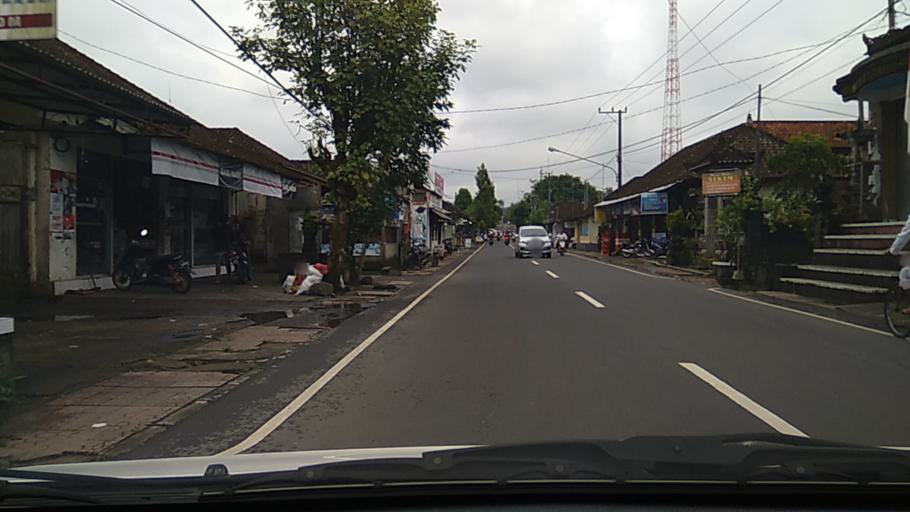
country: ID
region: Bali
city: Banjar Manukayaanyar
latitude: -8.4208
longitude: 115.3089
